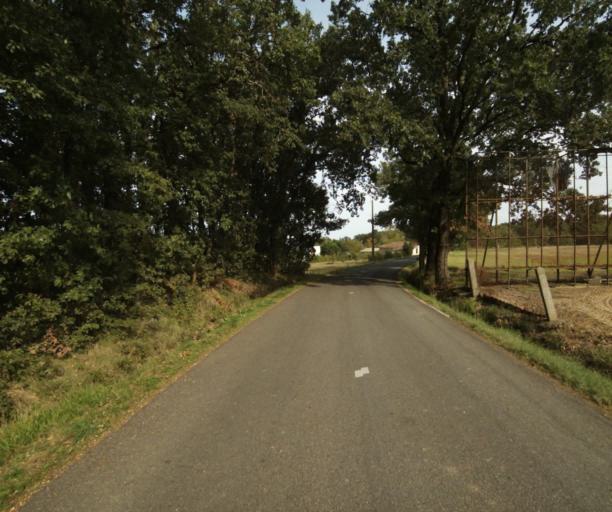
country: FR
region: Midi-Pyrenees
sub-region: Departement du Tarn-et-Garonne
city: Labastide-Saint-Pierre
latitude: 43.9081
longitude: 1.3855
